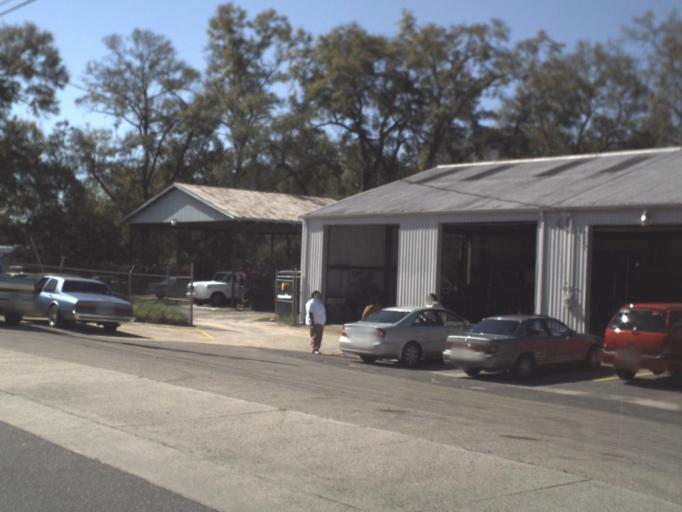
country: US
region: Florida
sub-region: Leon County
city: Tallahassee
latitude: 30.4045
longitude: -84.2835
